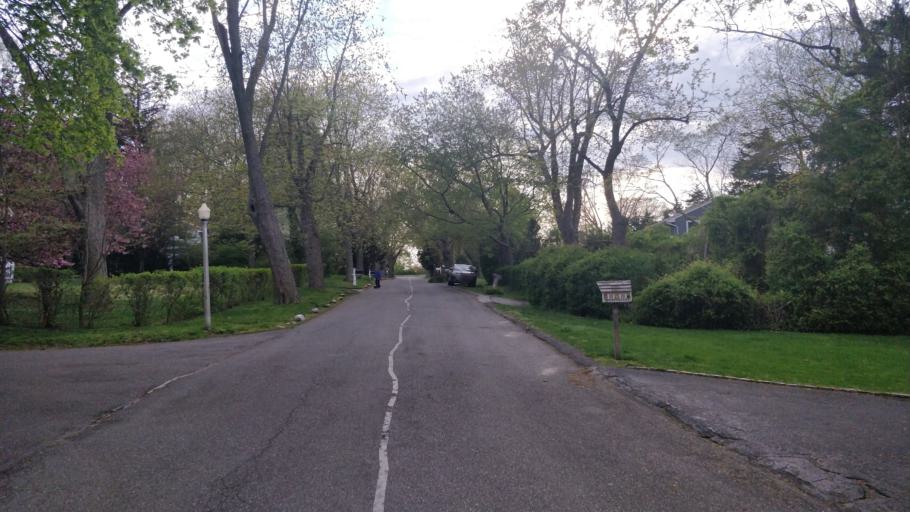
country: US
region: New York
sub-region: Suffolk County
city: Northport
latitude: 40.9105
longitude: -73.3425
